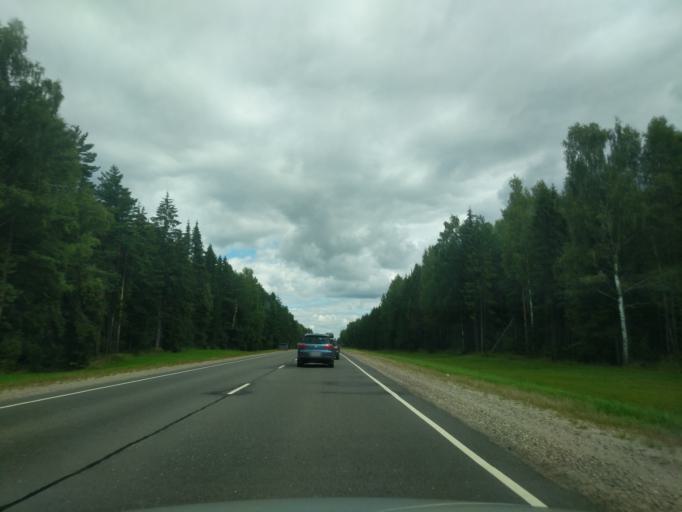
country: RU
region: Jaroslavl
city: Nekrasovskoye
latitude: 57.6012
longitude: 40.3177
